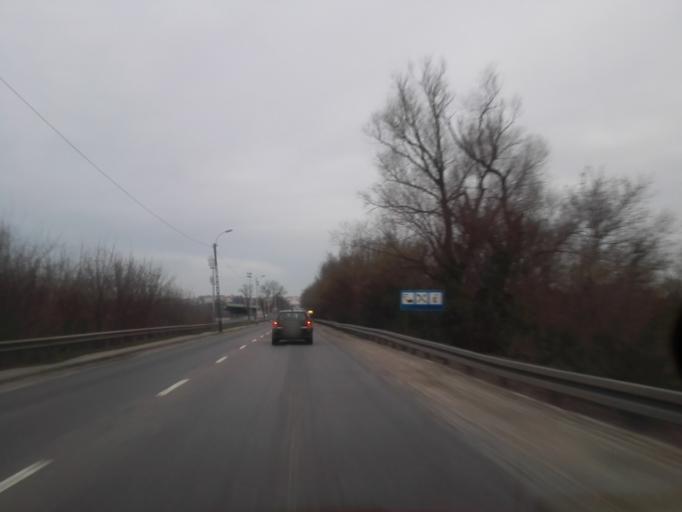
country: PL
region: Podlasie
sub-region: Powiat lomzynski
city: Piatnica
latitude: 53.1901
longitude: 22.0900
